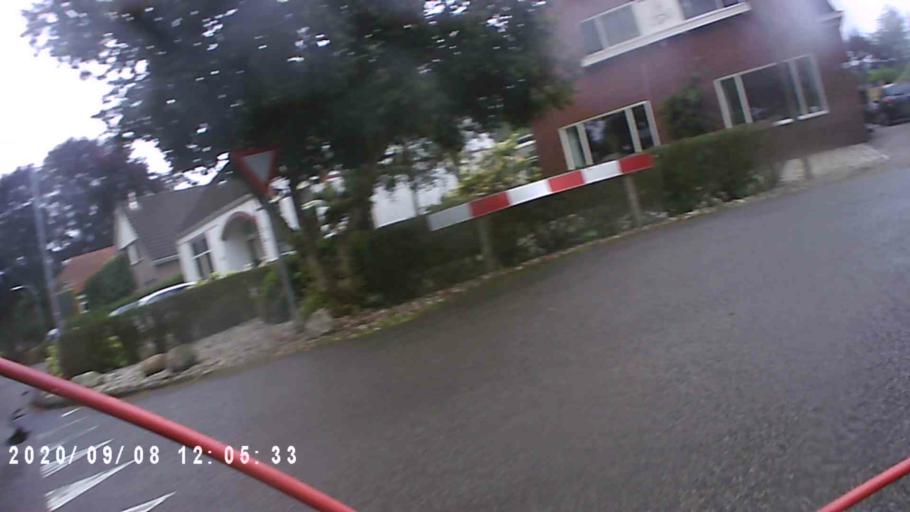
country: NL
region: Groningen
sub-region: Gemeente Veendam
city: Veendam
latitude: 53.1081
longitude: 6.8256
